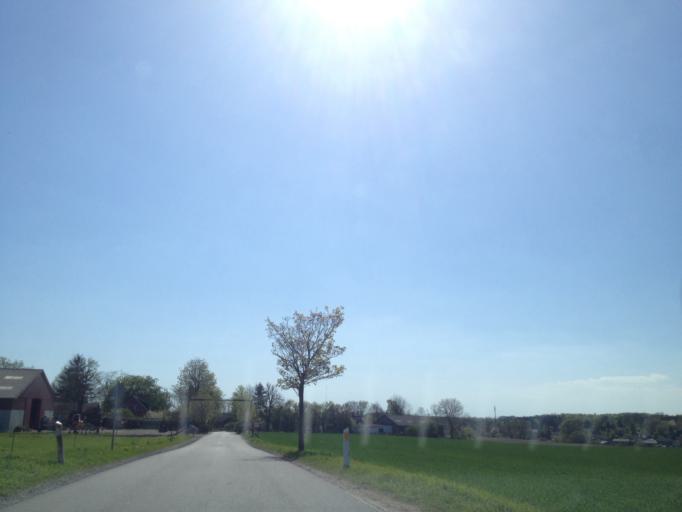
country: DK
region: Zealand
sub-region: Koge Kommune
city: Borup
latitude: 55.5110
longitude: 11.9915
